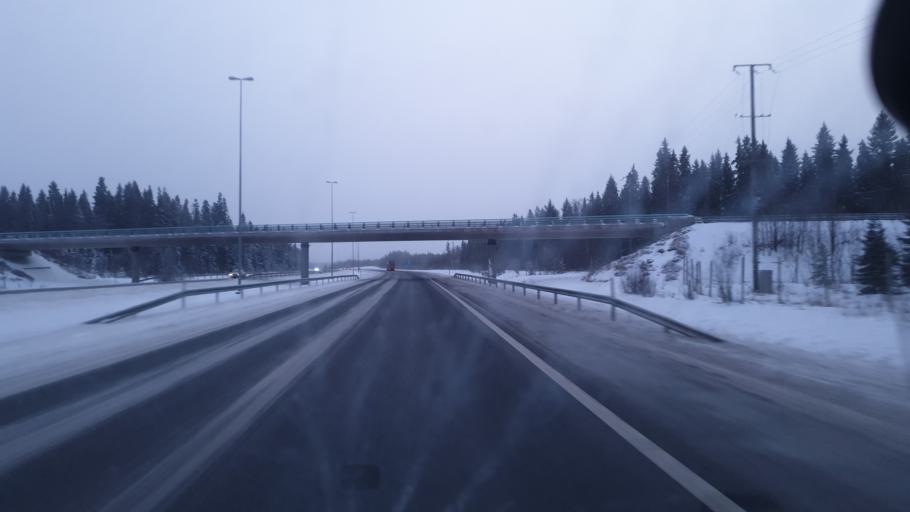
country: FI
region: Lapland
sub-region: Kemi-Tornio
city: Keminmaa
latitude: 65.8288
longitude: 24.3742
